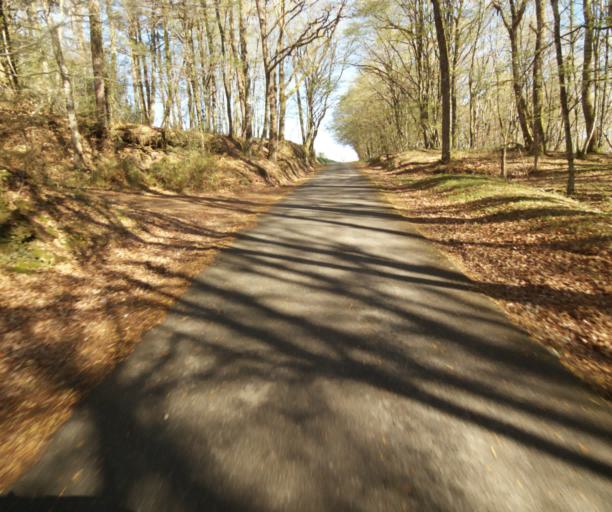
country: FR
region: Limousin
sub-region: Departement de la Correze
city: Laguenne
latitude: 45.2605
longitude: 1.8569
